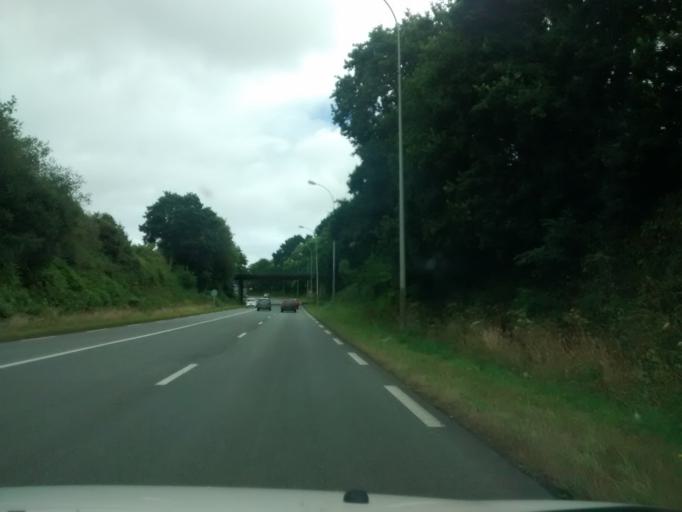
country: FR
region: Brittany
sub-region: Departement des Cotes-d'Armor
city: Lannion
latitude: 48.7398
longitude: -3.4656
